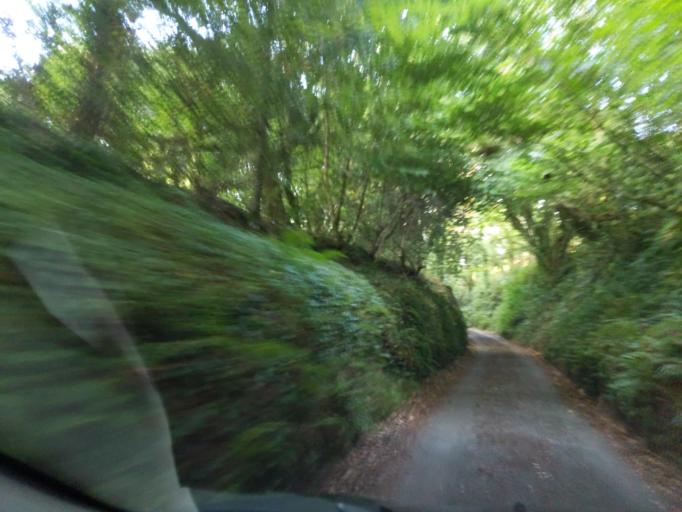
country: GB
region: England
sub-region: Cornwall
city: Fowey
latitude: 50.3641
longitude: -4.5973
